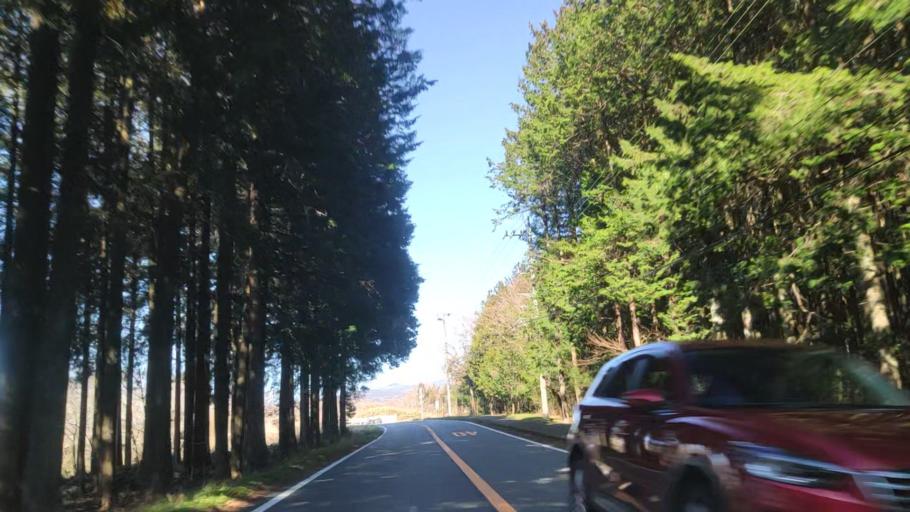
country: JP
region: Shizuoka
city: Fujinomiya
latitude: 35.3272
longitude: 138.5932
